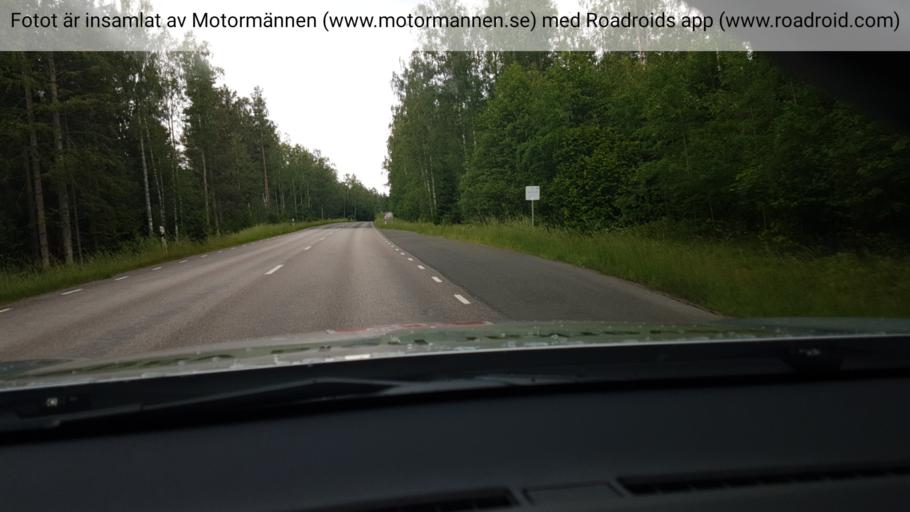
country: SE
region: Vaestra Goetaland
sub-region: Hjo Kommun
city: Hjo
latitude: 58.1792
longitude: 14.2039
